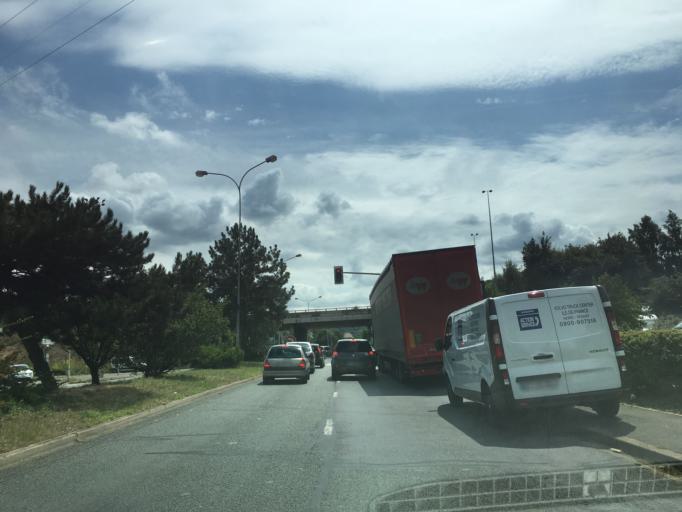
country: FR
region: Ile-de-France
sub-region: Departement du Val-de-Marne
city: Bonneuil-sur-Marne
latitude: 48.7592
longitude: 2.4807
